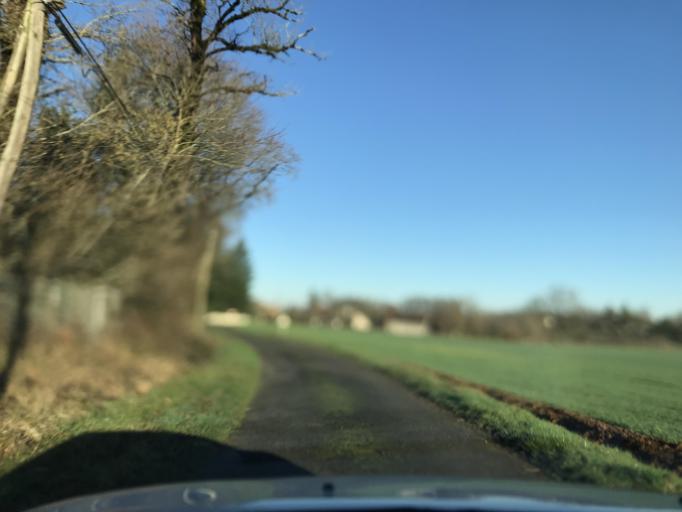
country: FR
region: Poitou-Charentes
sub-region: Departement de la Charente
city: Chasseneuil-sur-Bonnieure
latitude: 45.8463
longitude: 0.5019
